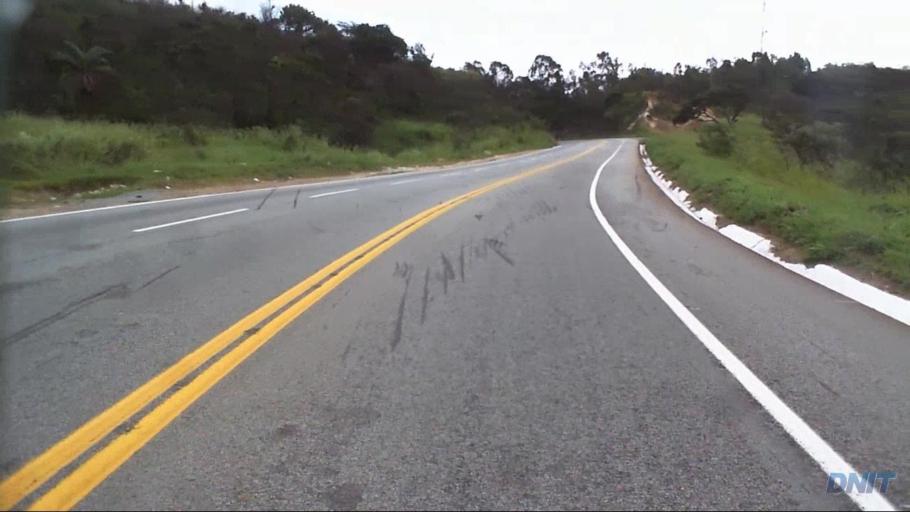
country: BR
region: Minas Gerais
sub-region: Caete
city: Caete
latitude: -19.7882
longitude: -43.6990
